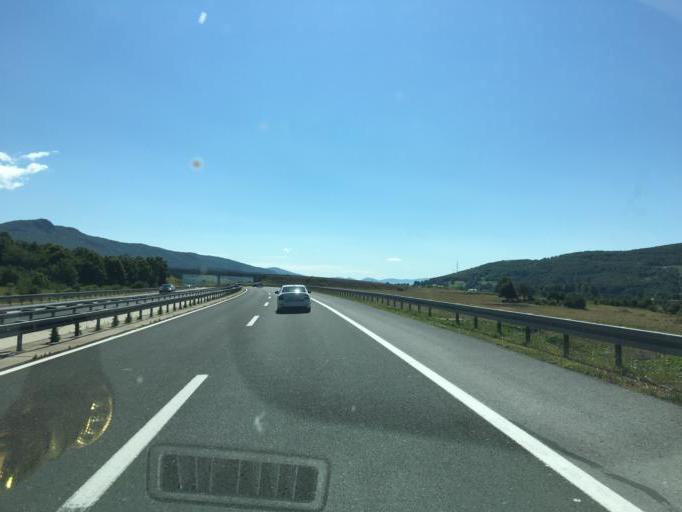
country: HR
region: Licko-Senjska
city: Brinje
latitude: 44.9496
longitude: 15.1446
